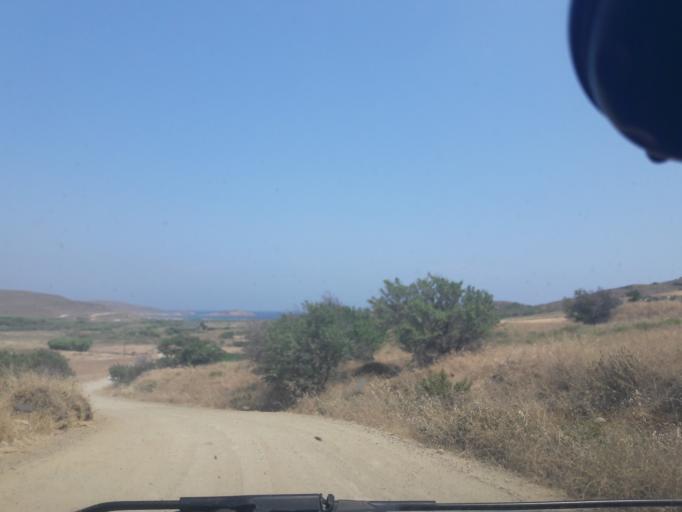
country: GR
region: North Aegean
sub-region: Nomos Lesvou
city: Myrina
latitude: 39.9775
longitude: 25.1500
